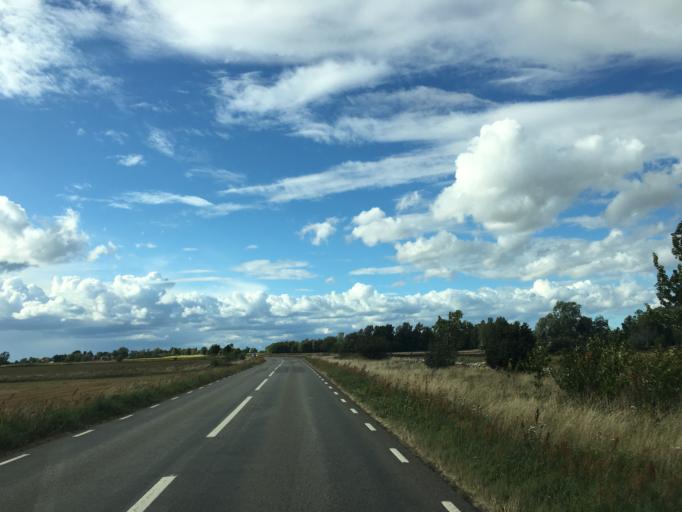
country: SE
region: Kalmar
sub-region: Morbylanga Kommun
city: Moerbylanga
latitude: 56.4349
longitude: 16.4349
